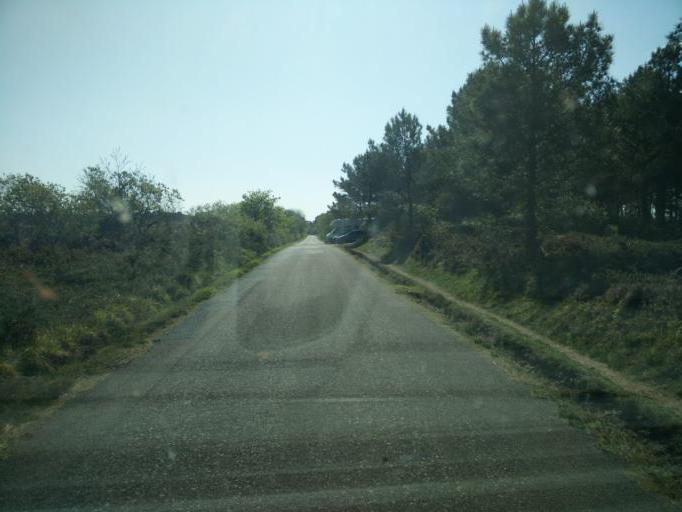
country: FR
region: Brittany
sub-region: Departement des Cotes-d'Armor
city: Erquy
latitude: 48.6389
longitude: -2.4785
